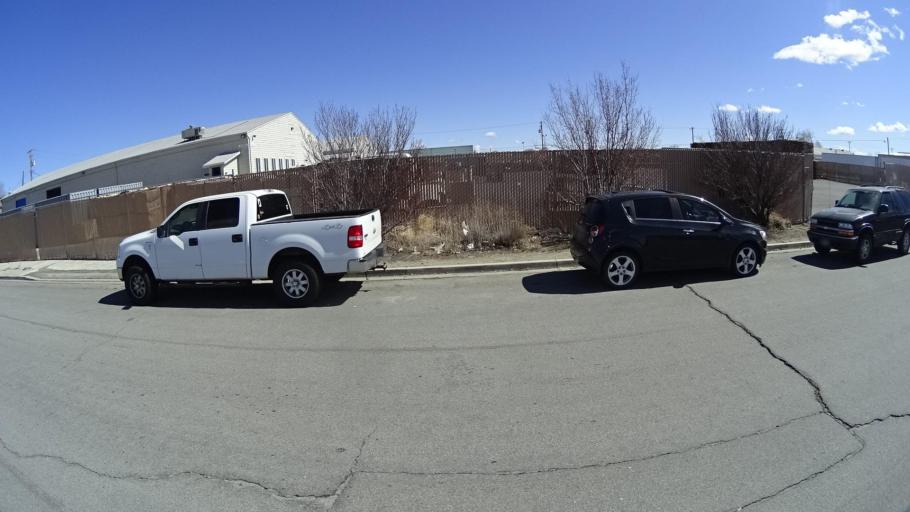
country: US
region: Nevada
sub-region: Washoe County
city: Lemmon Valley
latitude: 39.6552
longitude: -119.8864
